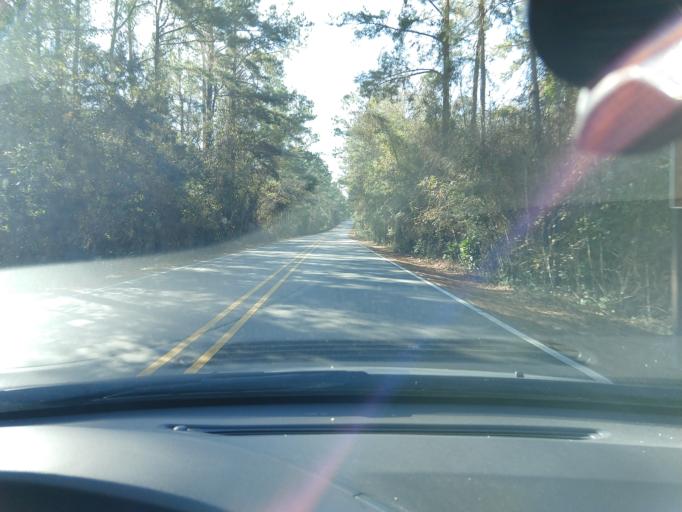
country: US
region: Mississippi
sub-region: Jackson County
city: Gulf Park Estates
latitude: 30.4023
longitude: -88.7780
